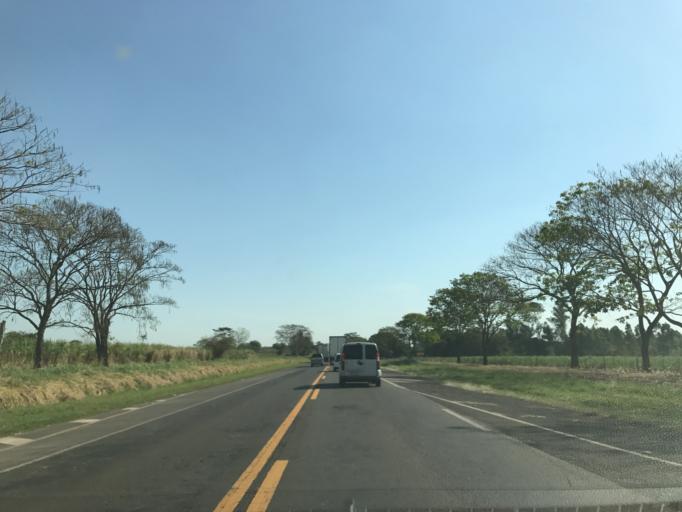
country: BR
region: Sao Paulo
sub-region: Penapolis
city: Penapolis
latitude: -21.4770
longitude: -50.1979
